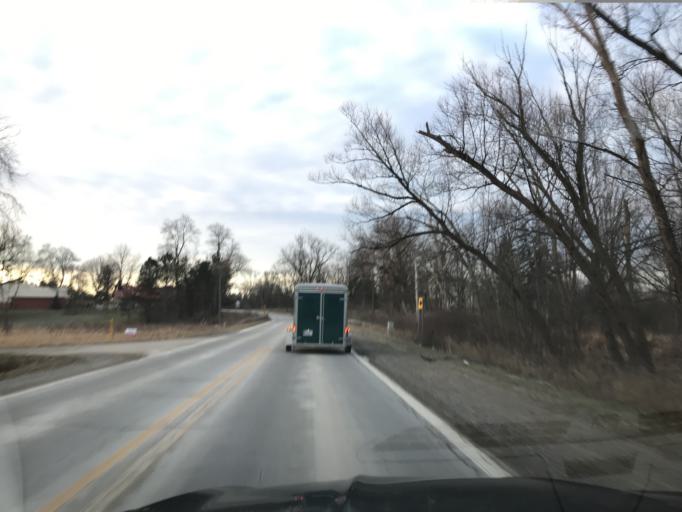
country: US
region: Michigan
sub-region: Macomb County
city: Armada
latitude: 42.8583
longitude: -82.8840
